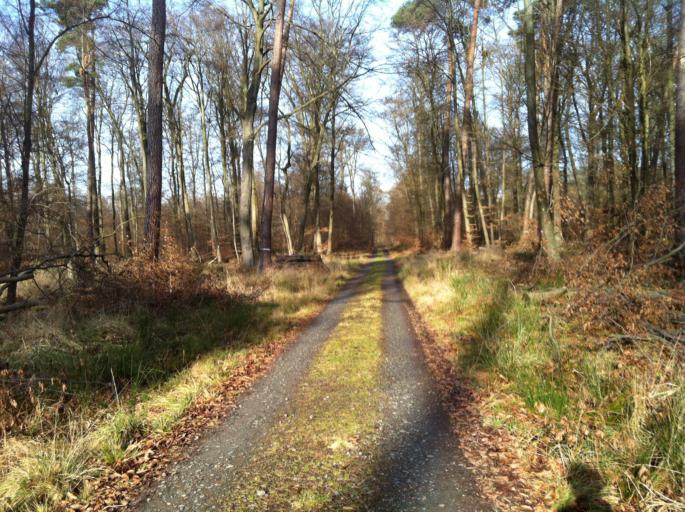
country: DE
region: Hesse
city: Langen
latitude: 50.0116
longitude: 8.6442
